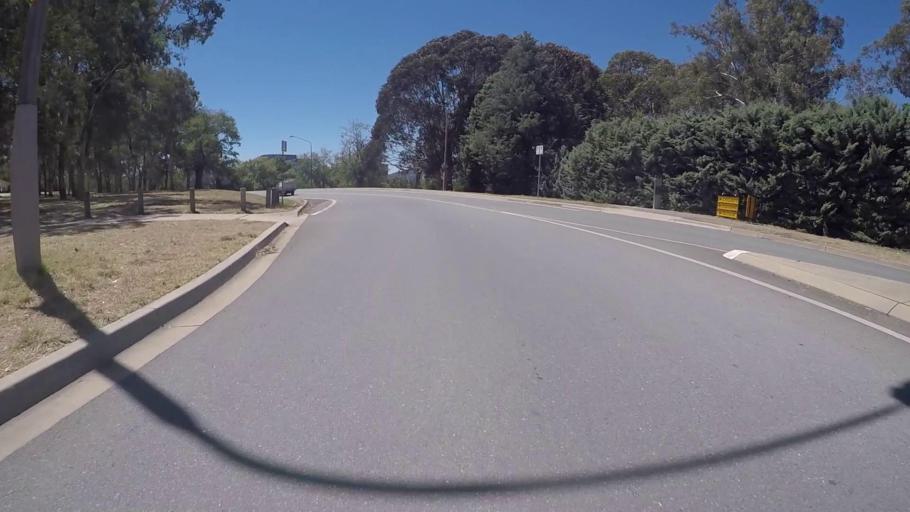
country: AU
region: Australian Capital Territory
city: Canberra
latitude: -35.2903
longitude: 149.1181
